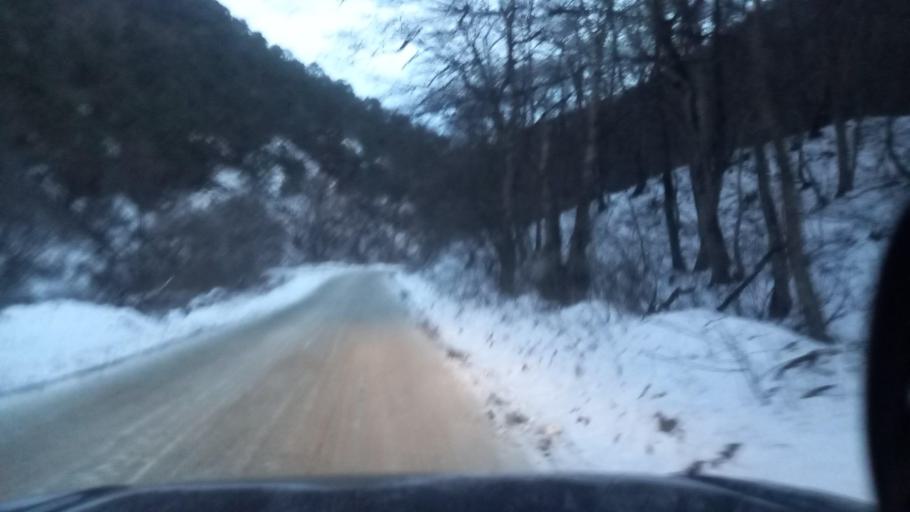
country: RU
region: Ingushetiya
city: Dzhayrakh
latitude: 42.8256
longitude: 44.5932
